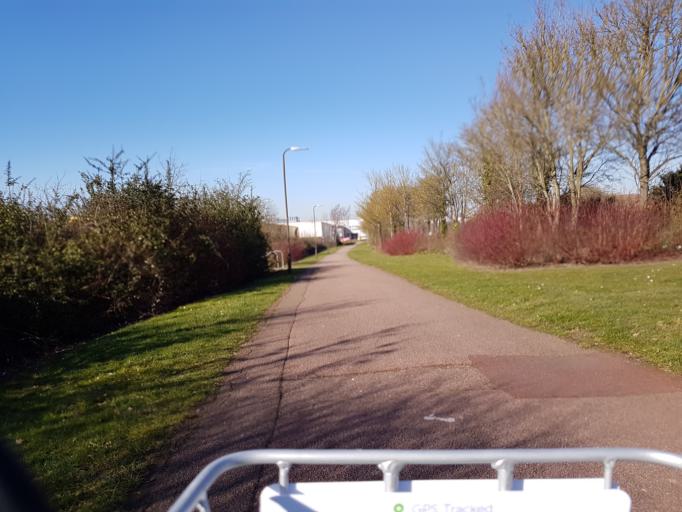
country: GB
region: England
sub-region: Milton Keynes
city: Milton Keynes
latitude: 52.0263
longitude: -0.7600
